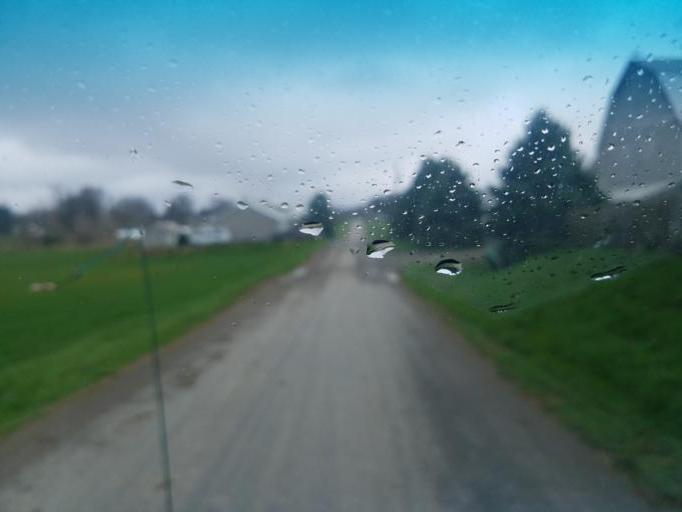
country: US
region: Ohio
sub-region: Richland County
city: Shelby
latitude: 40.9194
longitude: -82.5952
